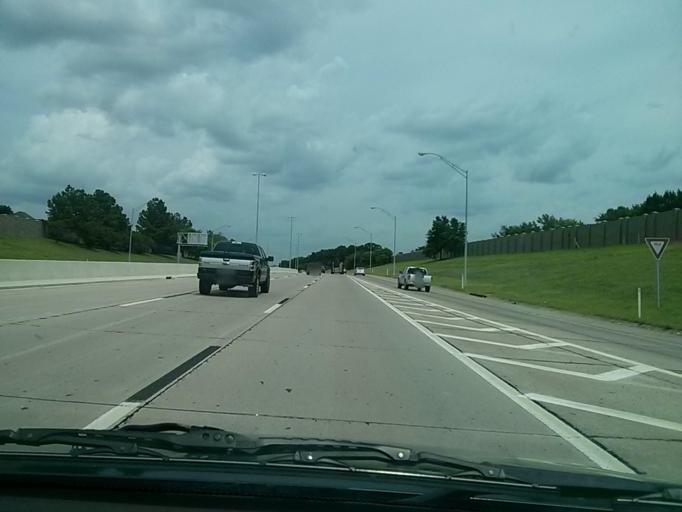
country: US
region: Oklahoma
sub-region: Tulsa County
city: Jenks
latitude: 36.0252
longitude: -95.9179
